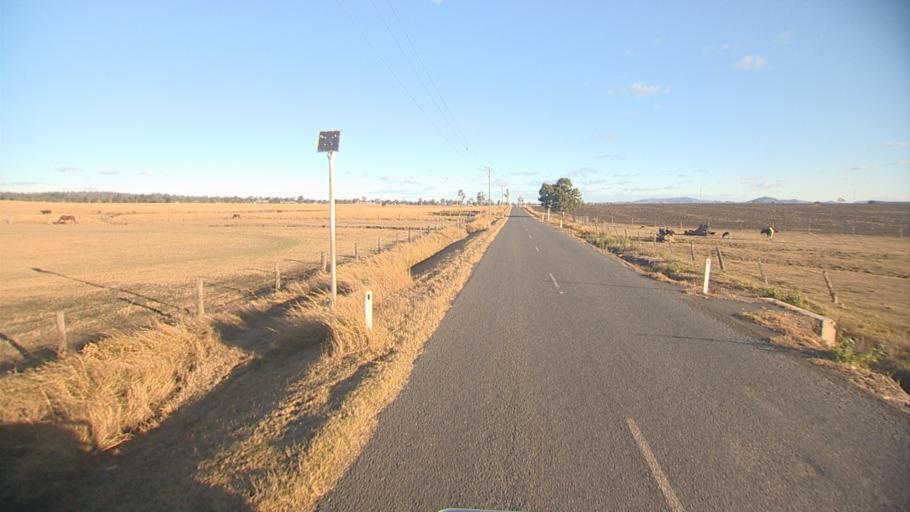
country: AU
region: Queensland
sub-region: Logan
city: Cedar Vale
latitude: -27.8613
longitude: 152.9589
